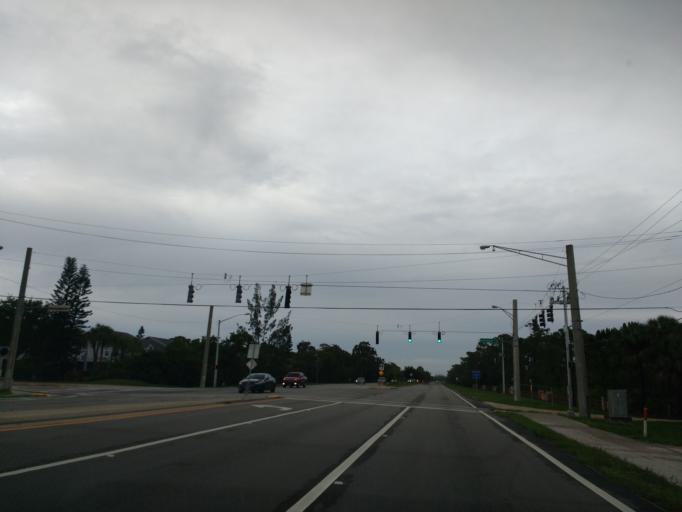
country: US
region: Florida
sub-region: Lee County
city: Cypress Lake
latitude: 26.5292
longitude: -81.8870
